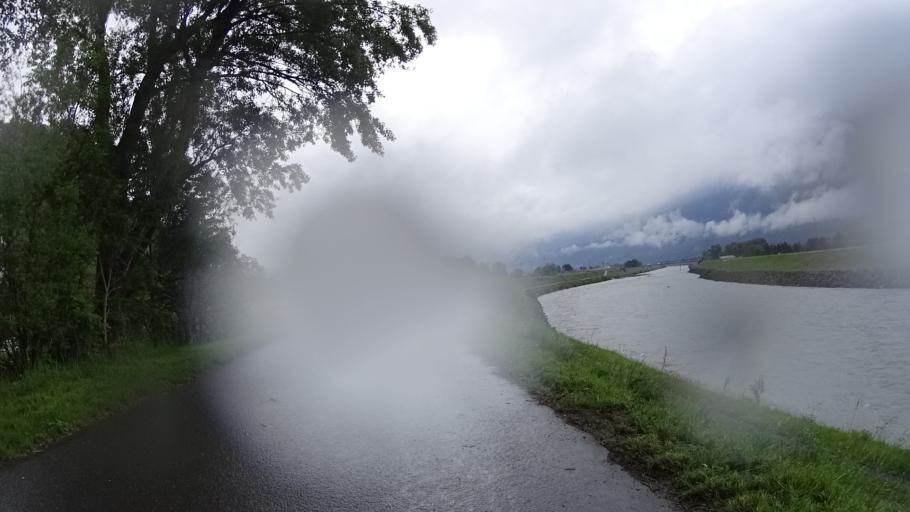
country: LI
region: Balzers
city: Balzers
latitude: 47.0650
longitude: 9.4714
